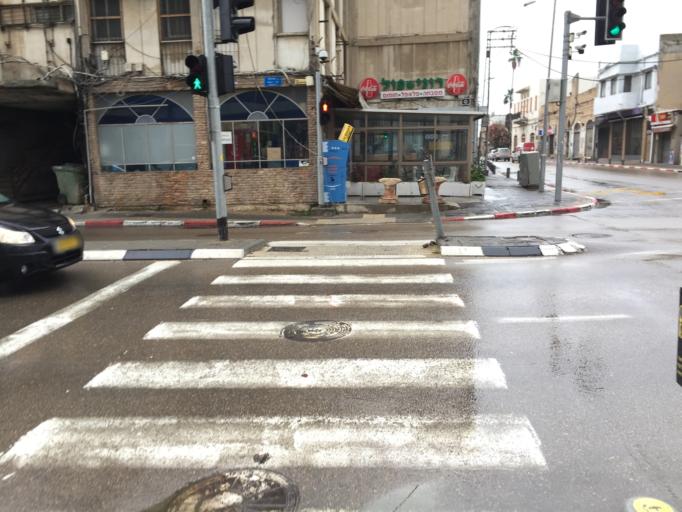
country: IL
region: Tel Aviv
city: Yafo
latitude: 32.0579
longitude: 34.7642
